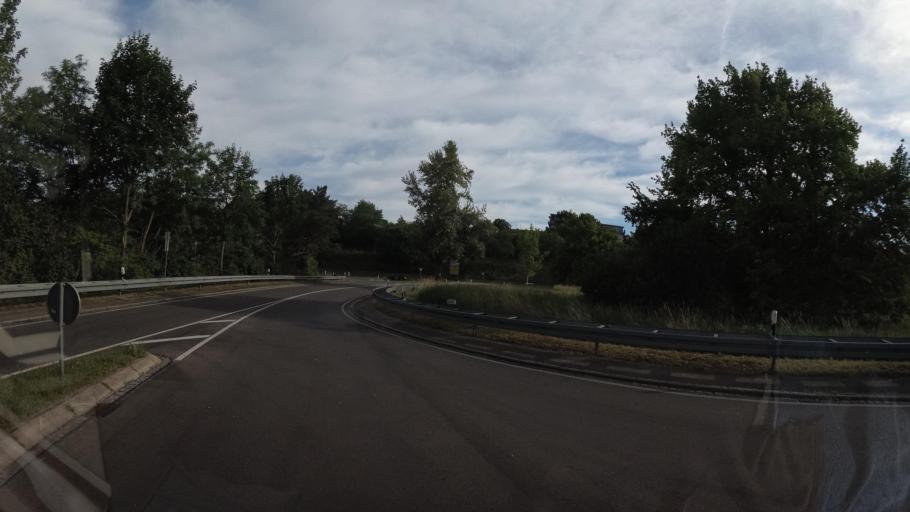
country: DE
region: Baden-Wuerttemberg
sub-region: Freiburg Region
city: Weil am Rhein
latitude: 47.5877
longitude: 7.6220
